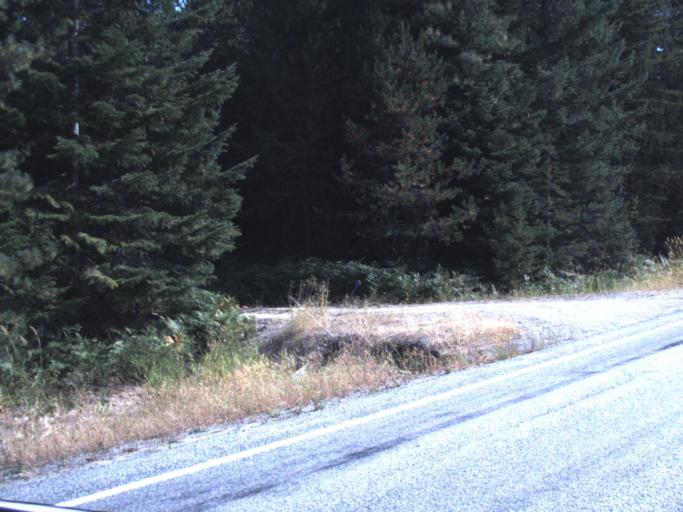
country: US
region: Washington
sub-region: Pend Oreille County
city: Newport
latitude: 48.2787
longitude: -117.2846
